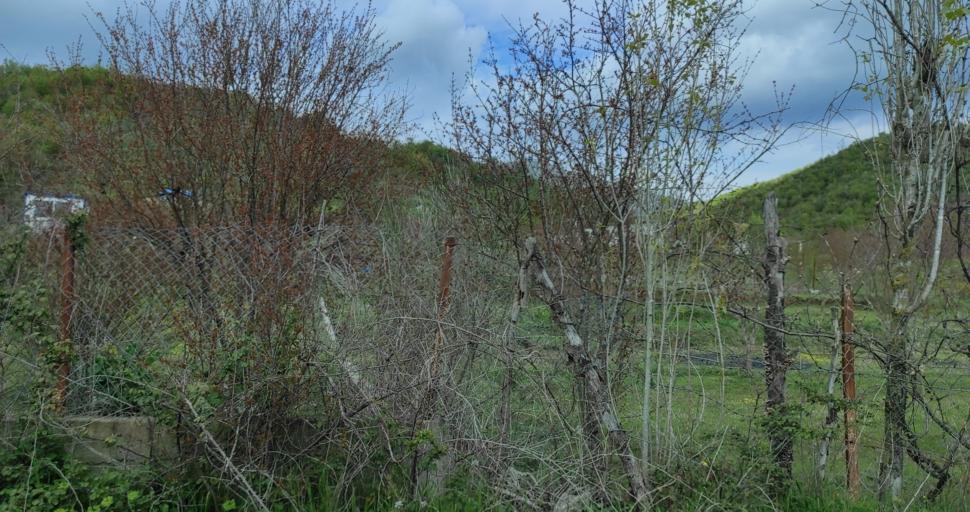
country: AL
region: Shkoder
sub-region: Rrethi i Shkodres
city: Dajc
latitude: 42.0289
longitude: 19.4173
